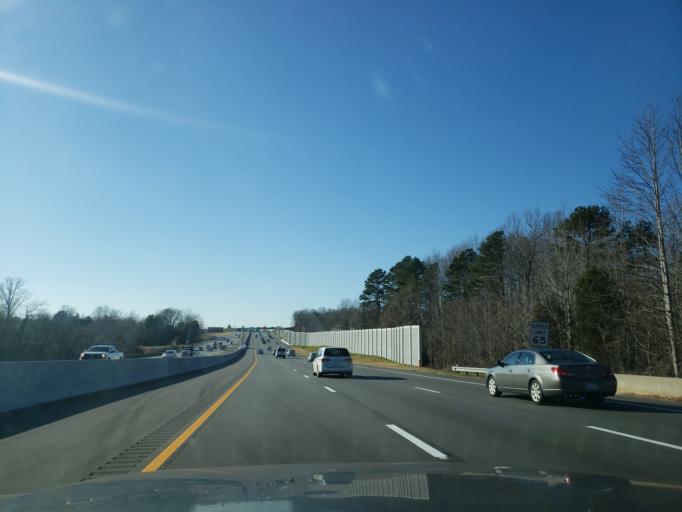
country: US
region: North Carolina
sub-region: Forsyth County
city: Clemmons
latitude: 36.0729
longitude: -80.3473
